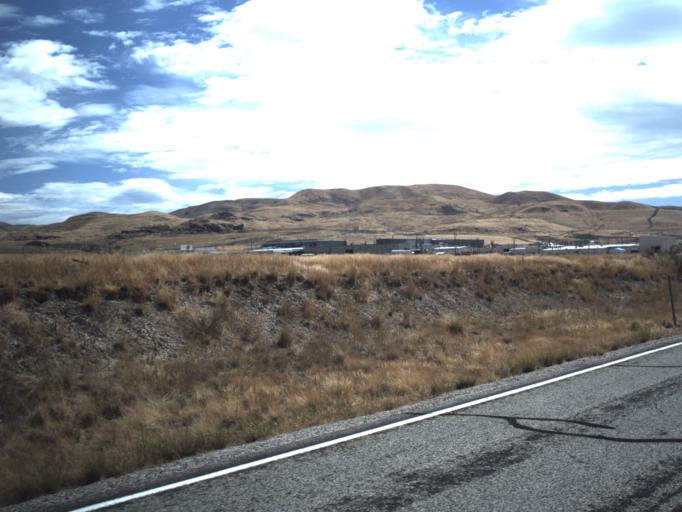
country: US
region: Utah
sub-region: Box Elder County
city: Tremonton
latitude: 41.7261
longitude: -112.4338
